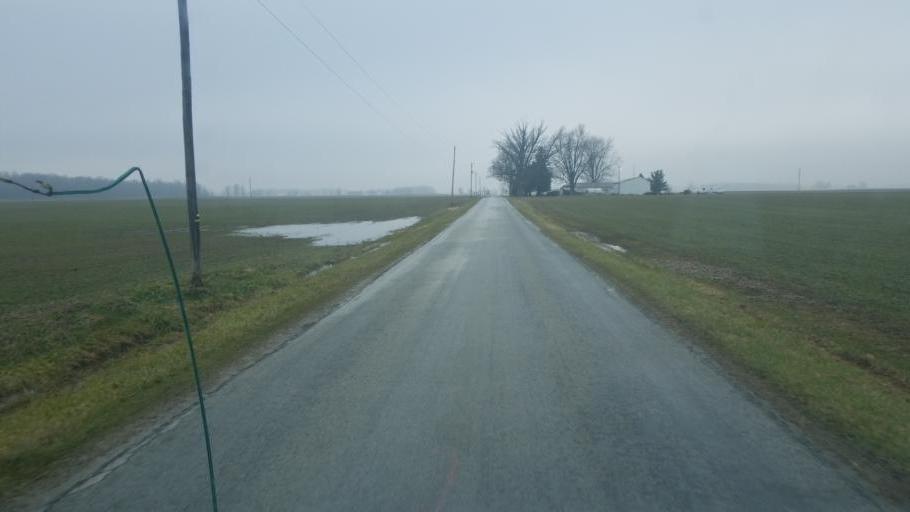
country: US
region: Ohio
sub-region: Hardin County
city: Kenton
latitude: 40.6694
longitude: -83.4776
